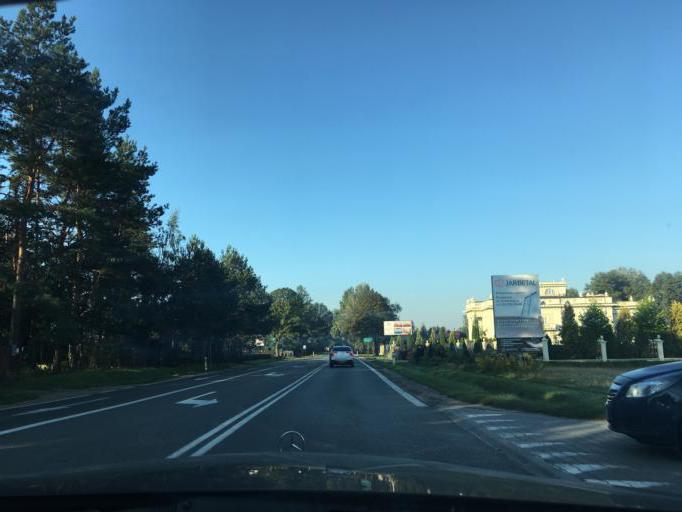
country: PL
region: Masovian Voivodeship
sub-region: Powiat pruszkowski
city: Otrebusy
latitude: 52.1346
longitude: 20.7638
